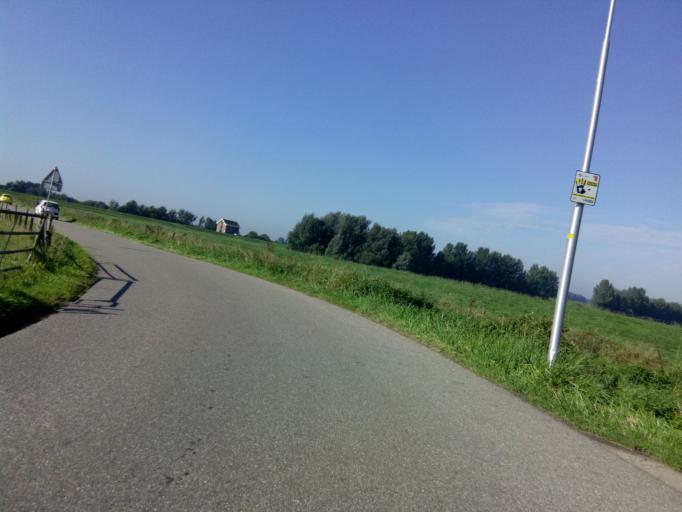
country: NL
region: Gelderland
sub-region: Gemeente Buren
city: Lienden
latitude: 51.9788
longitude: 5.4957
